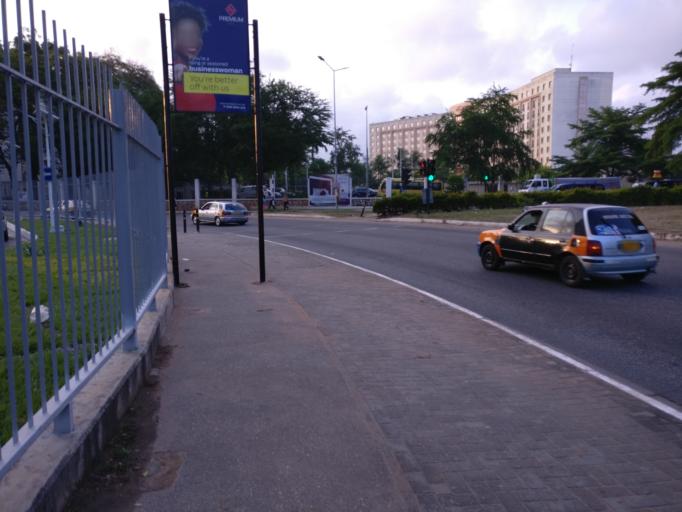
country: GH
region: Greater Accra
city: Accra
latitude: 5.5521
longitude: -0.2029
